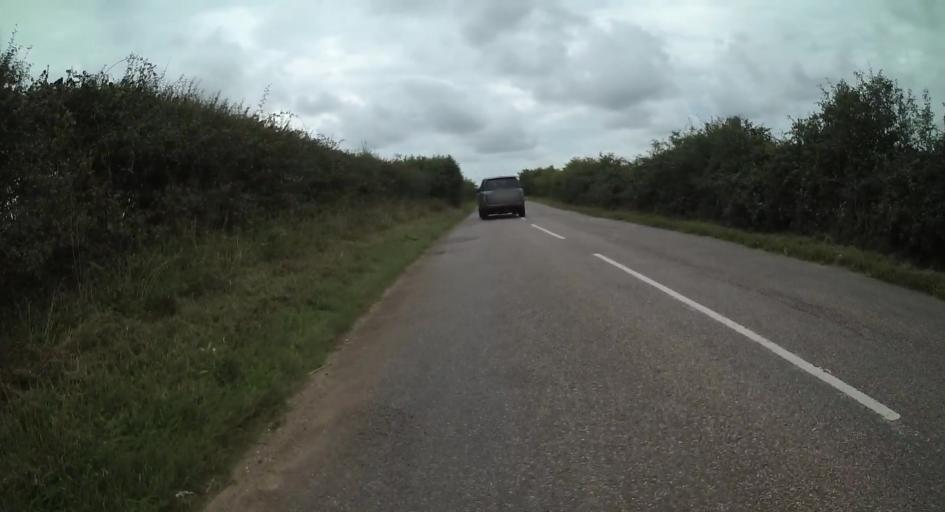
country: GB
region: England
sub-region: Isle of Wight
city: Niton
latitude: 50.6243
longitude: -1.2642
